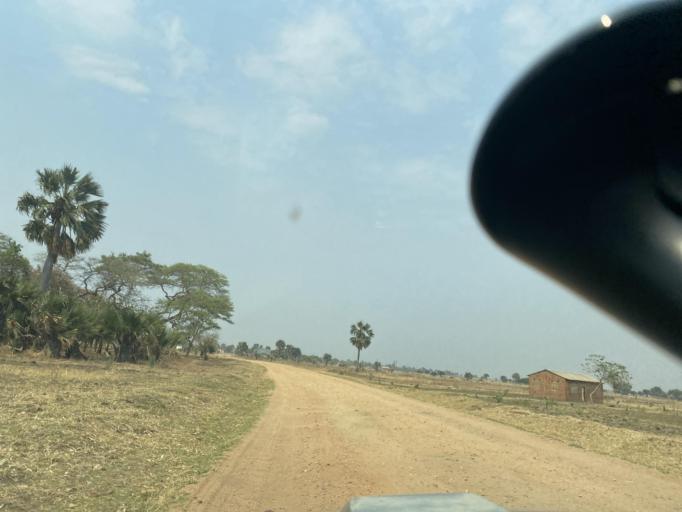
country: ZM
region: Lusaka
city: Kafue
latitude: -15.6496
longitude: 28.0322
